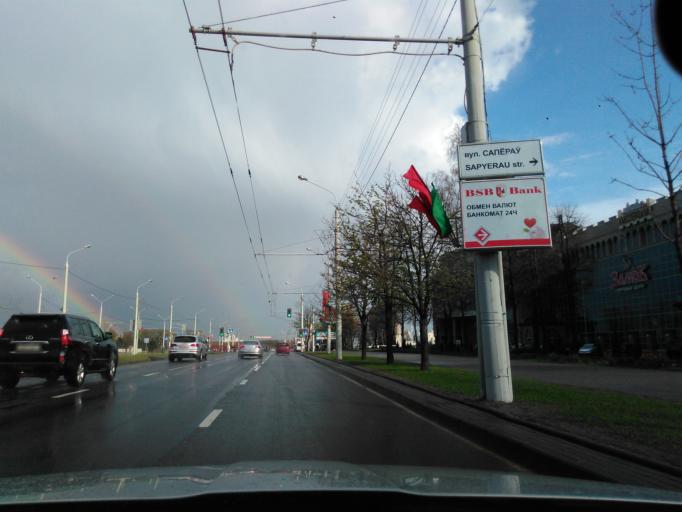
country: BY
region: Minsk
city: Minsk
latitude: 53.9275
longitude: 27.5176
